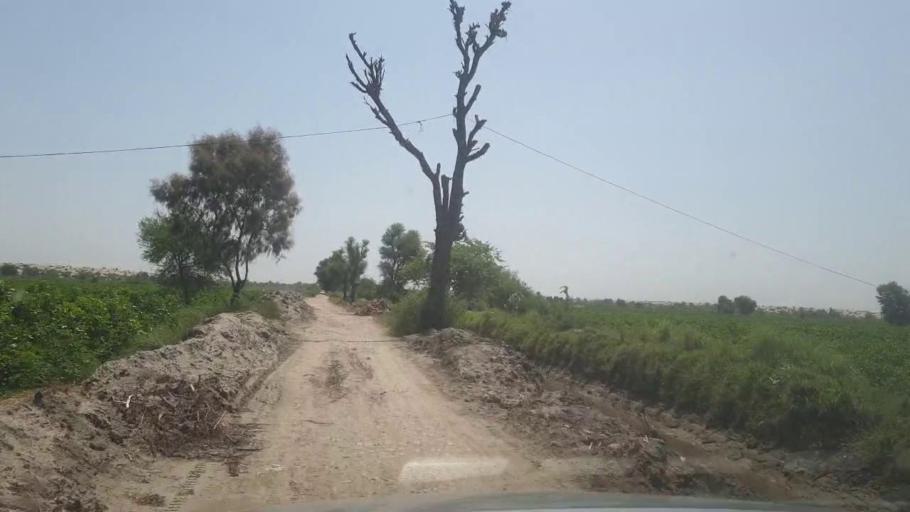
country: PK
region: Sindh
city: Khairpur
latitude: 27.3515
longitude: 69.0496
